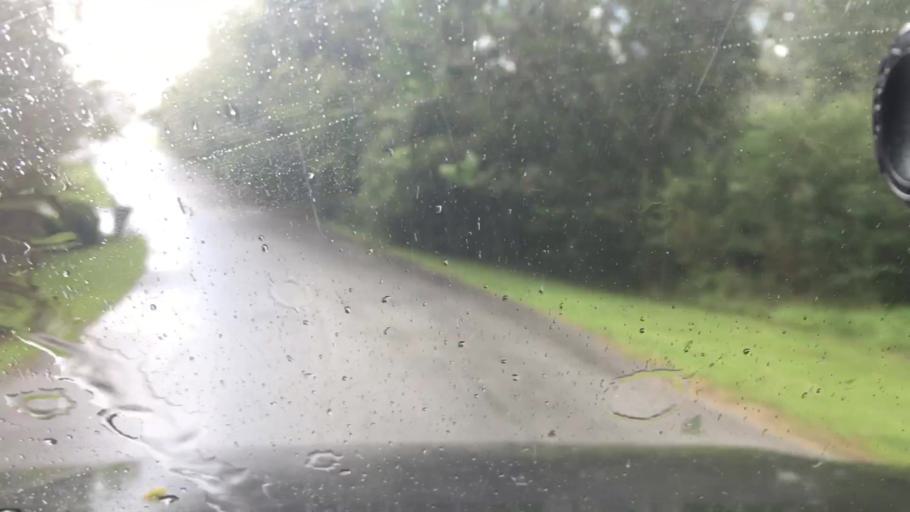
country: US
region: Georgia
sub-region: Bibb County
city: West Point
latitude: 32.8189
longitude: -83.7952
